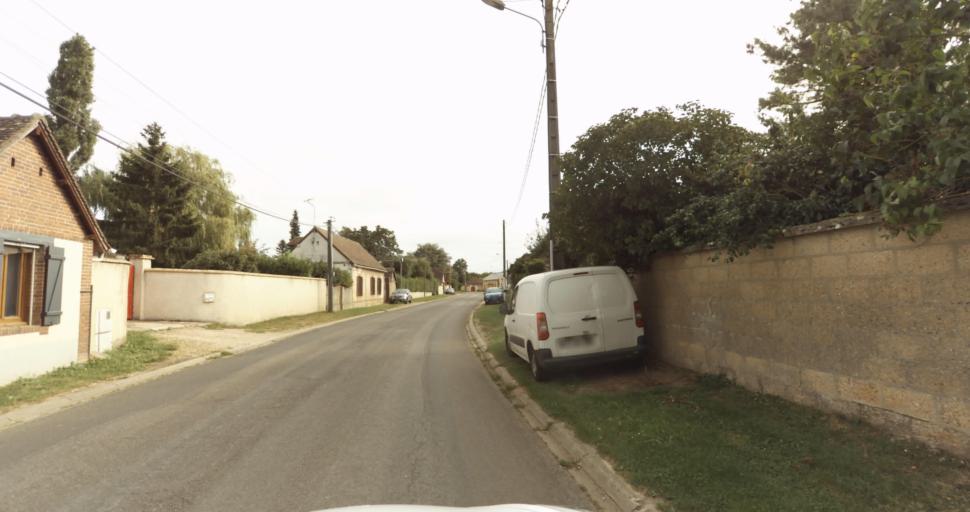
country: FR
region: Haute-Normandie
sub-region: Departement de l'Eure
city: La Madeleine-de-Nonancourt
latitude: 48.8608
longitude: 1.2432
